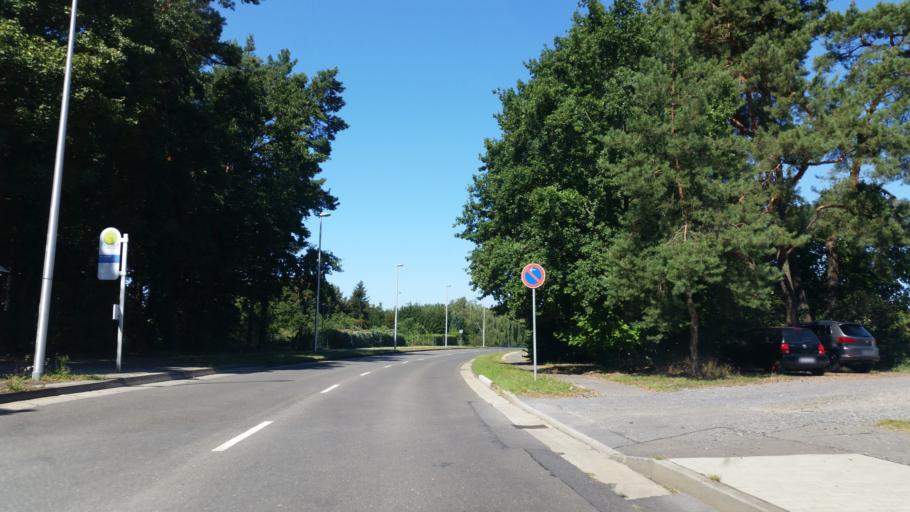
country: DE
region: Brandenburg
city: Cottbus
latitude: 51.7300
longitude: 14.3134
